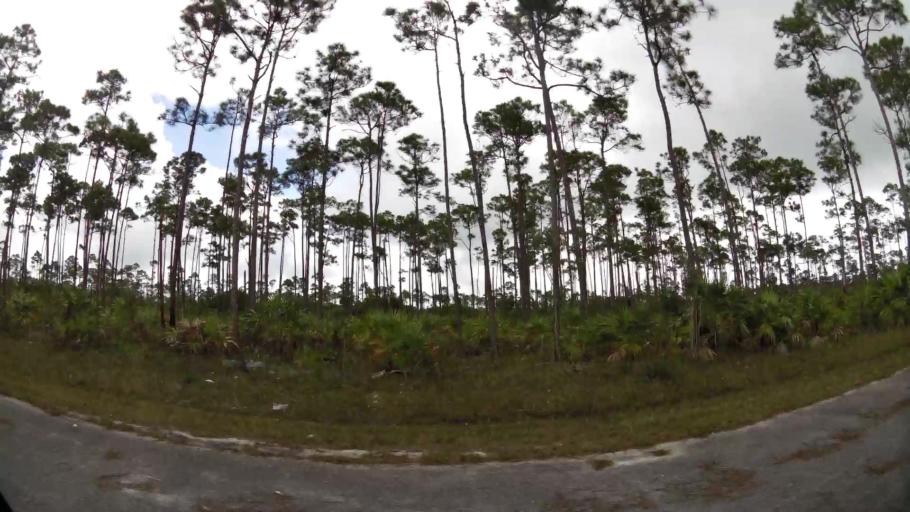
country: BS
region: Freeport
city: Lucaya
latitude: 26.5606
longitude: -78.5775
